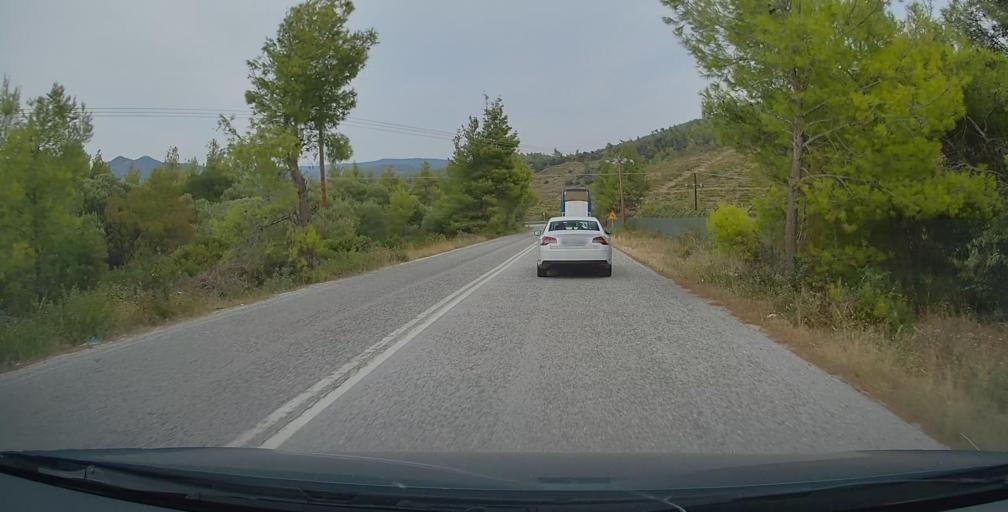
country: GR
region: Central Macedonia
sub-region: Nomos Chalkidikis
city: Neos Marmaras
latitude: 40.0642
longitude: 23.8077
